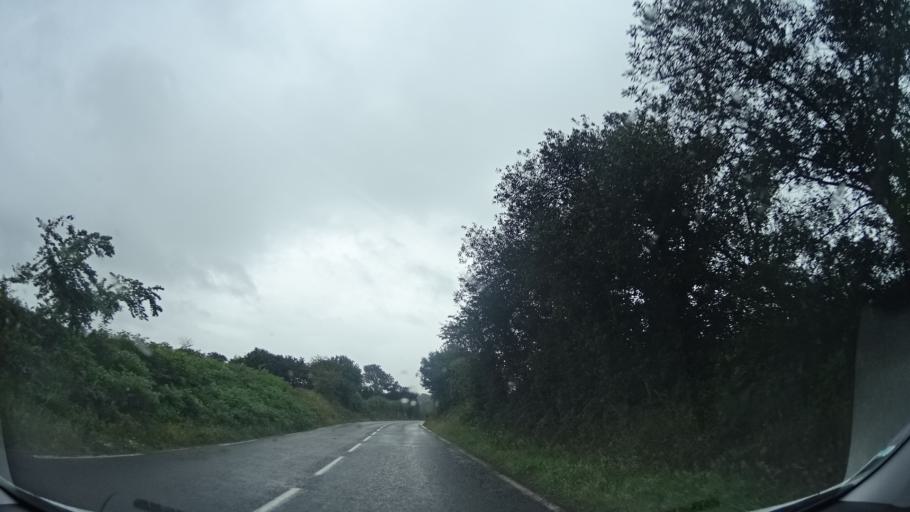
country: FR
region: Lower Normandy
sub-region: Departement de la Manche
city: Beaumont-Hague
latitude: 49.6058
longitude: -1.7870
